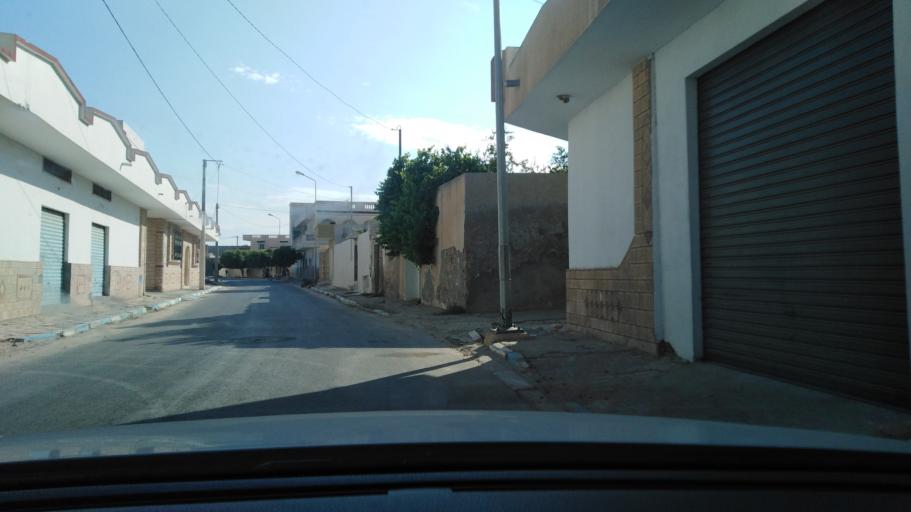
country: TN
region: Qabis
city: Gabes
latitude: 33.9397
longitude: 10.0702
